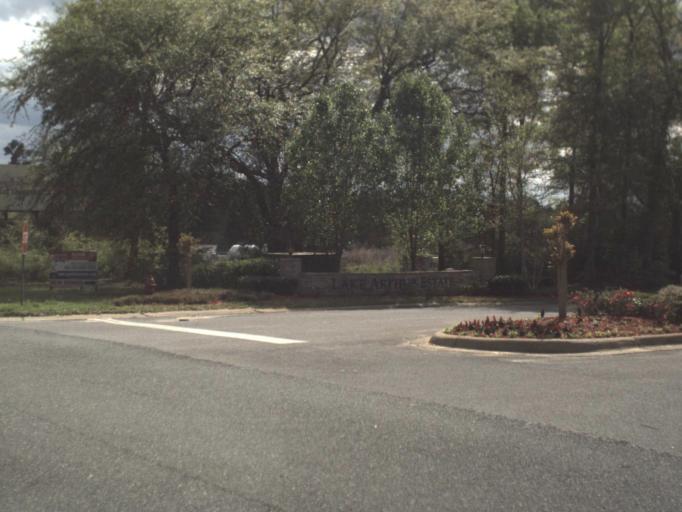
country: US
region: Florida
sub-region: Okaloosa County
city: Crestview
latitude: 30.8445
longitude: -86.5293
